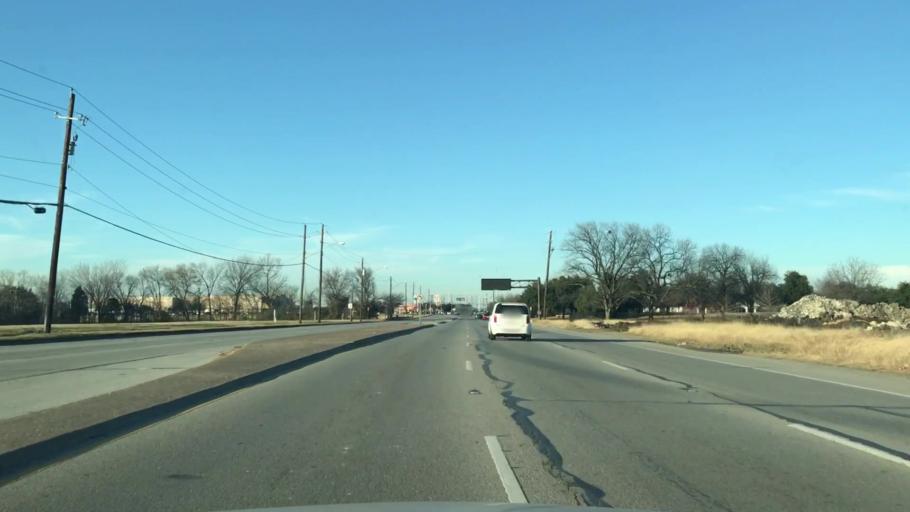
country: US
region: Texas
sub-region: Dallas County
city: Balch Springs
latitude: 32.7880
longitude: -96.6851
